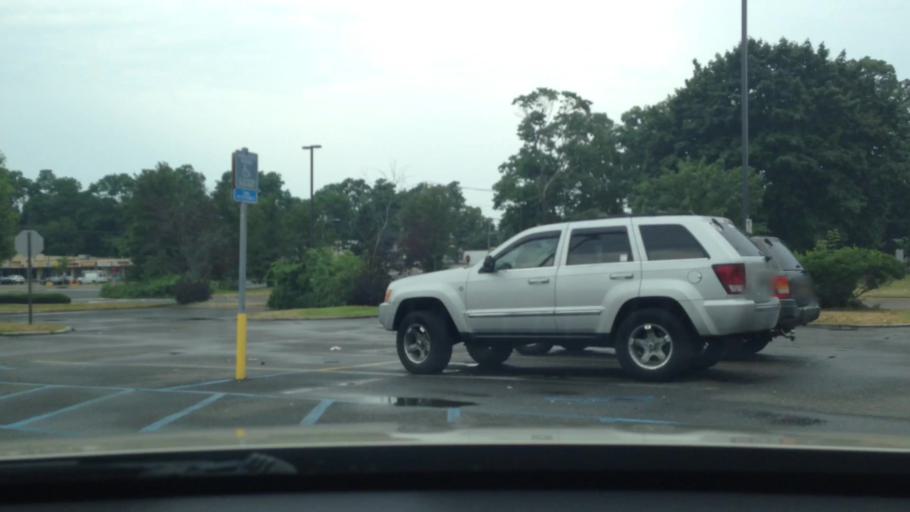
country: US
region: New York
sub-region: Suffolk County
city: Selden
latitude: 40.8673
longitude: -73.0350
